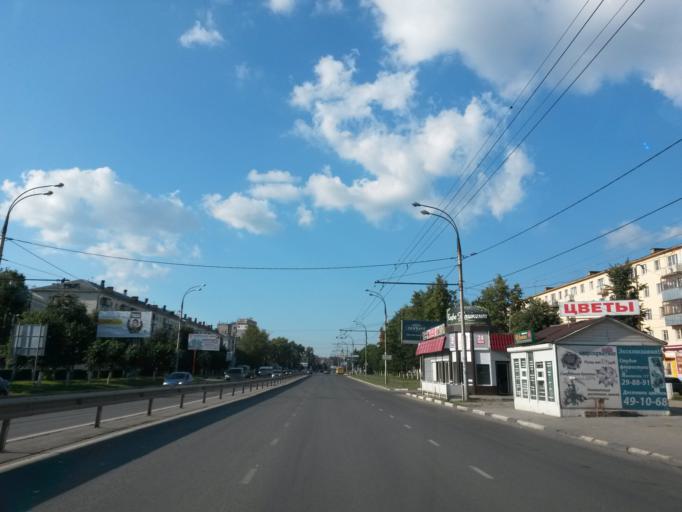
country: RU
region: Ivanovo
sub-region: Gorod Ivanovo
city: Ivanovo
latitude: 56.9654
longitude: 40.9735
